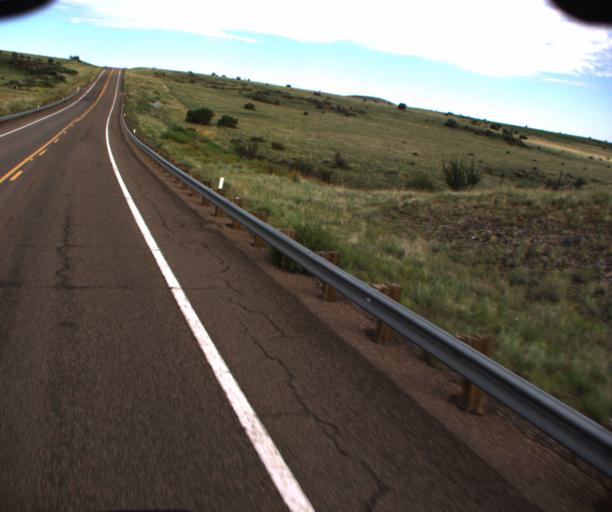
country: US
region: Arizona
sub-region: Apache County
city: Springerville
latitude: 34.2228
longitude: -109.4845
